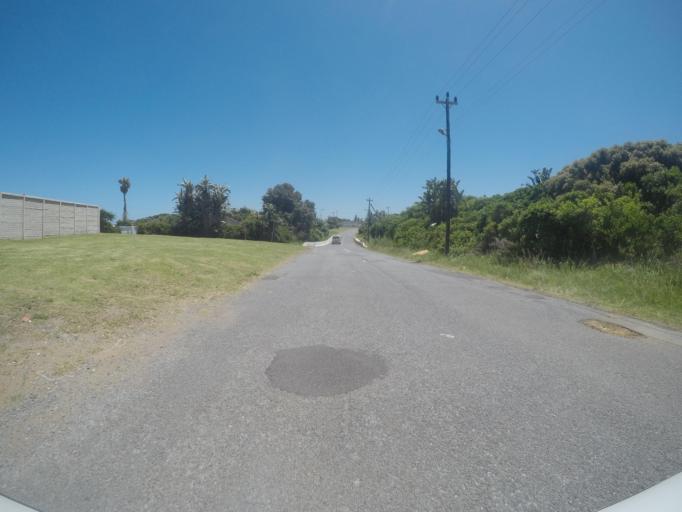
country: ZA
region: Eastern Cape
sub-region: Buffalo City Metropolitan Municipality
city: East London
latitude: -32.9540
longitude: 28.0052
